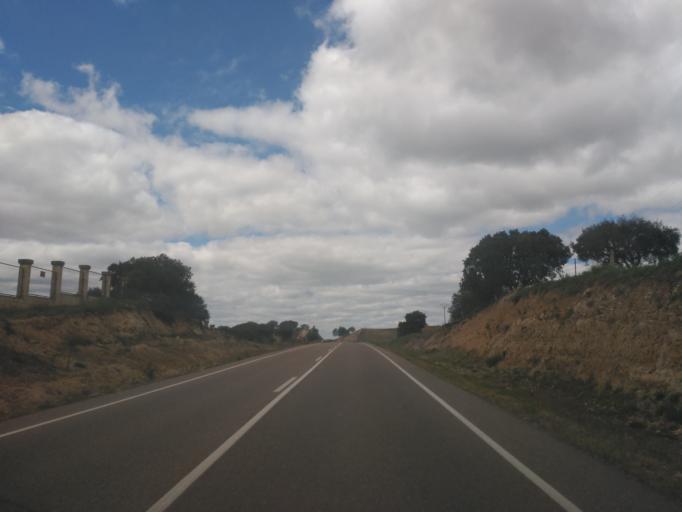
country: ES
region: Castille and Leon
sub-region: Provincia de Salamanca
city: Florida de Liebana
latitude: 41.0328
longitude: -5.7321
